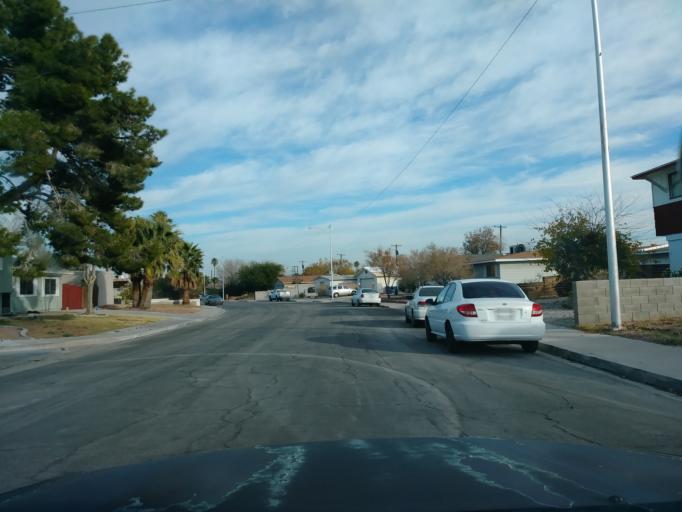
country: US
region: Nevada
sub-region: Clark County
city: Spring Valley
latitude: 36.1699
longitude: -115.2290
